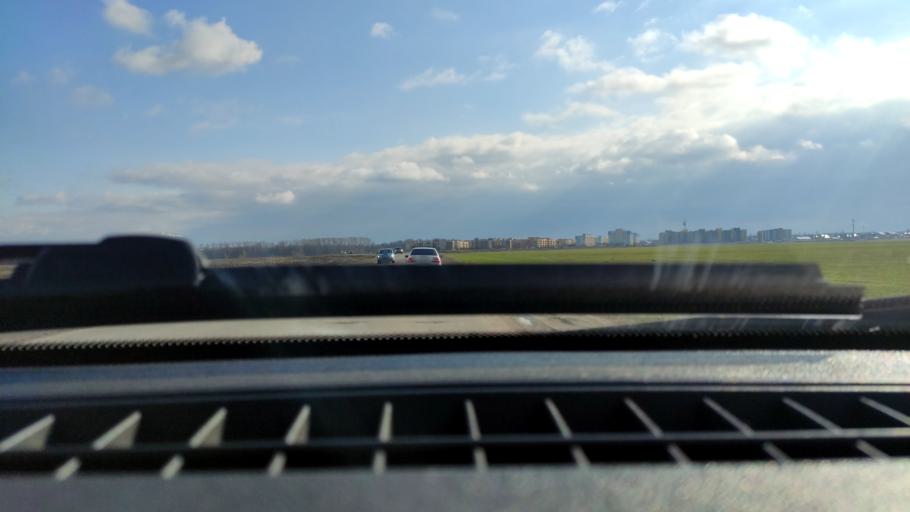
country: RU
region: Bashkortostan
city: Ufa
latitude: 54.8064
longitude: 55.9650
